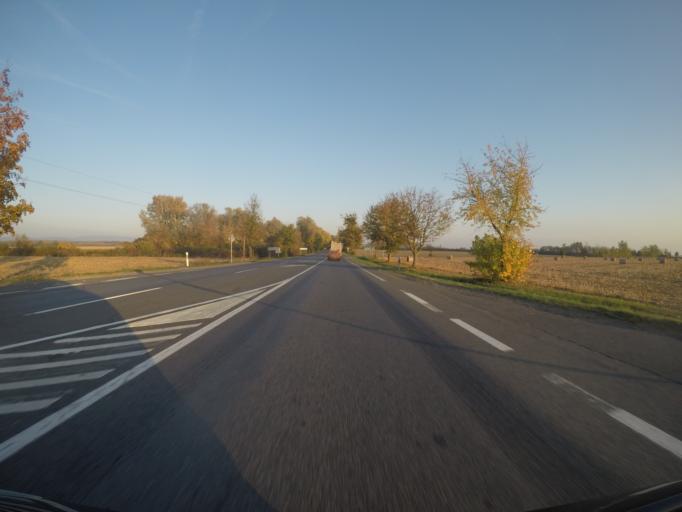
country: HU
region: Baranya
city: Szentlorinc
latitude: 46.0405
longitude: 17.9267
